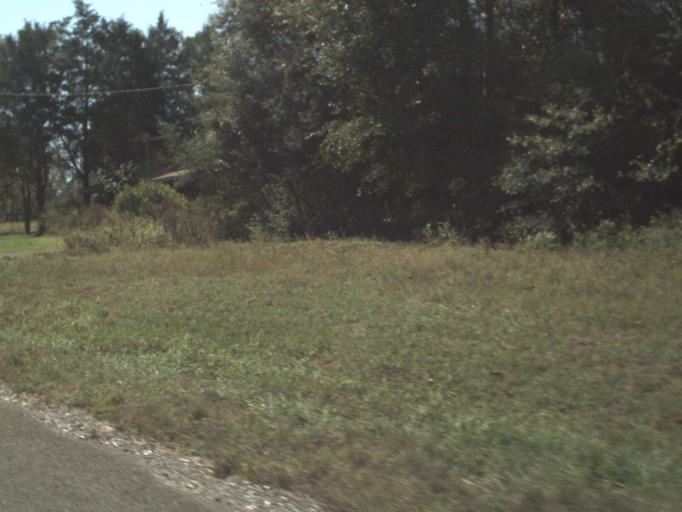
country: US
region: Florida
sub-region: Walton County
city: DeFuniak Springs
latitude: 30.8995
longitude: -86.1300
